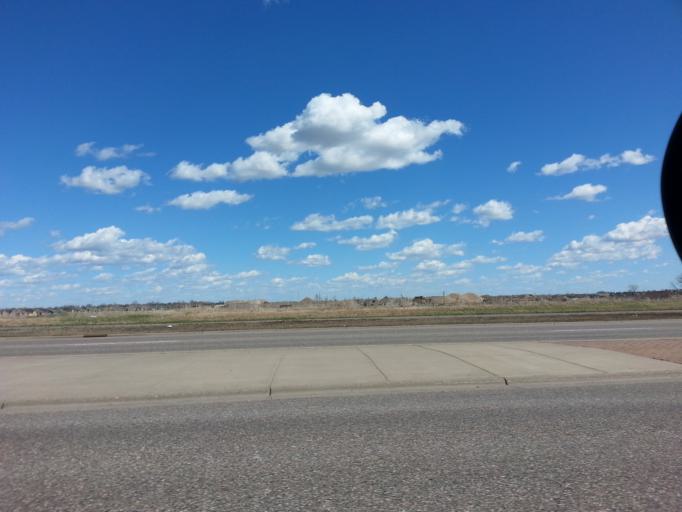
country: US
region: Minnesota
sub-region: Dakota County
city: Apple Valley
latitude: 44.7155
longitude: -93.1770
